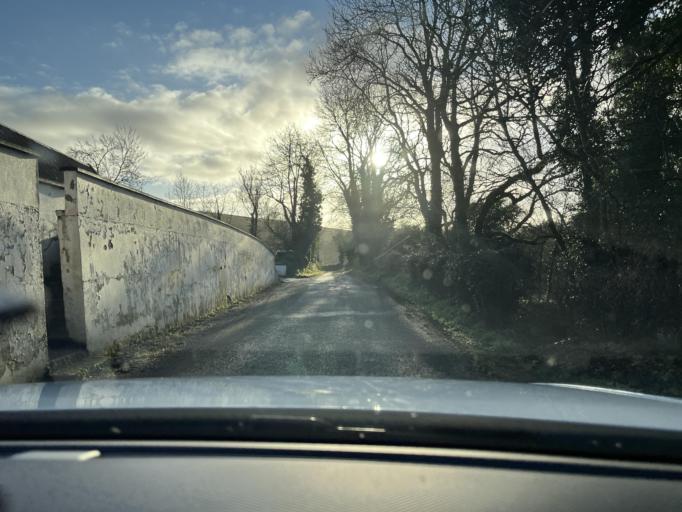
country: IE
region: Connaught
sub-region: County Leitrim
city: Manorhamilton
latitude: 54.2105
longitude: -7.9680
